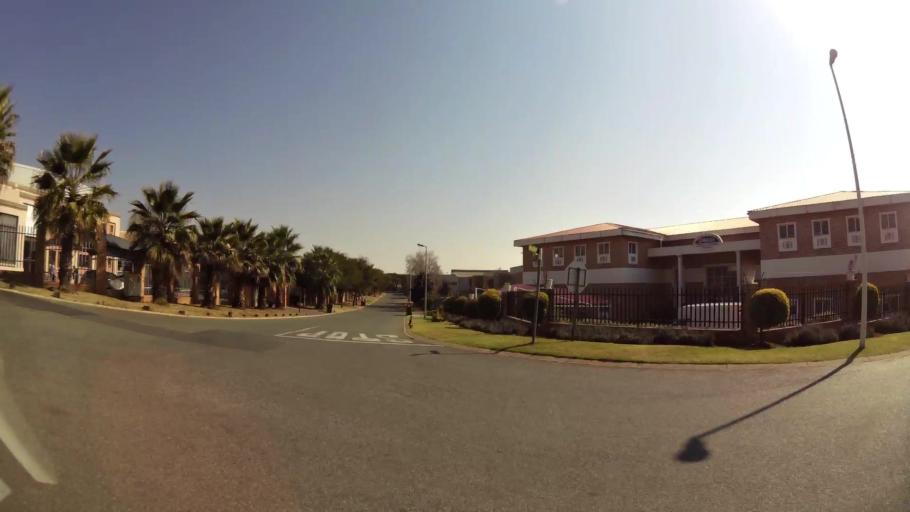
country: ZA
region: Gauteng
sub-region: City of Johannesburg Metropolitan Municipality
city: Modderfontein
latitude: -26.1132
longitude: 28.1398
